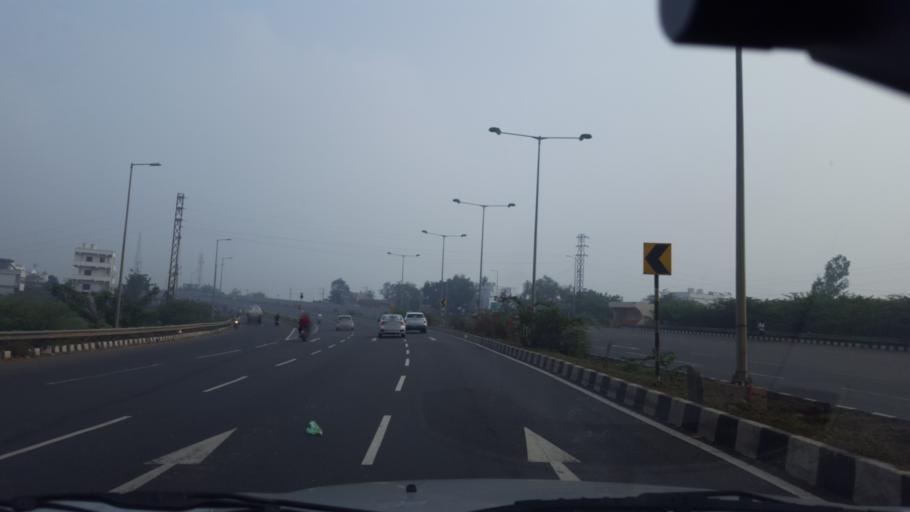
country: IN
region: Andhra Pradesh
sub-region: Prakasam
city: Ongole
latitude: 15.5486
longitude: 80.0555
